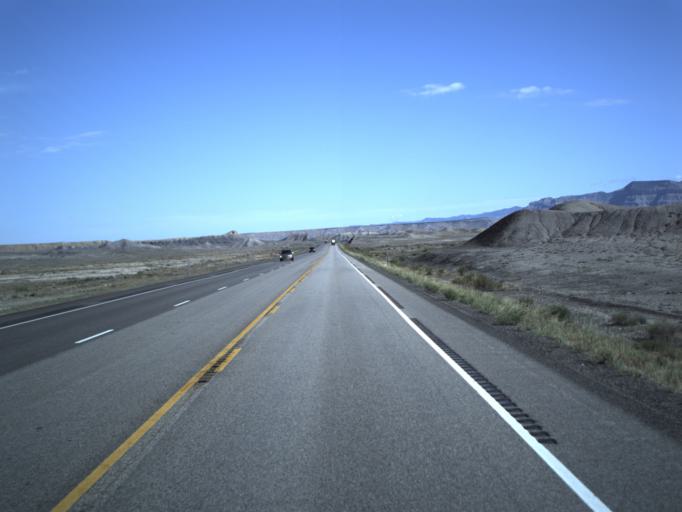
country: US
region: Utah
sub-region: Carbon County
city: East Carbon City
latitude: 39.3127
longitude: -110.3617
